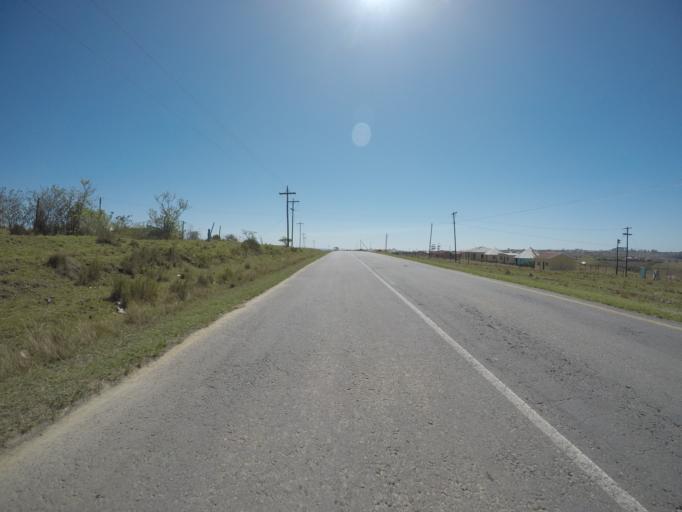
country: ZA
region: Eastern Cape
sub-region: OR Tambo District Municipality
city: Libode
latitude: -31.9105
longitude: 28.9964
